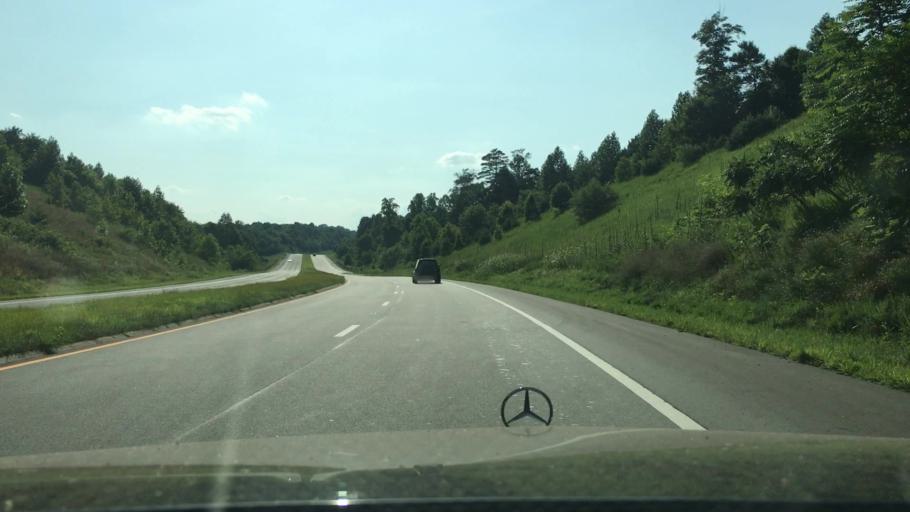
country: US
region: Virginia
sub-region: Amherst County
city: Madison Heights
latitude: 37.4139
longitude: -79.0993
